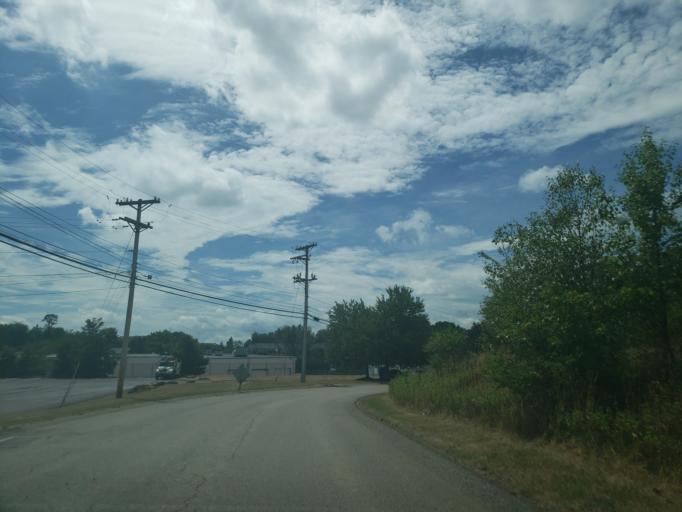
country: US
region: Pennsylvania
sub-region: Allegheny County
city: Coraopolis
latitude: 40.5316
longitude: -80.1369
